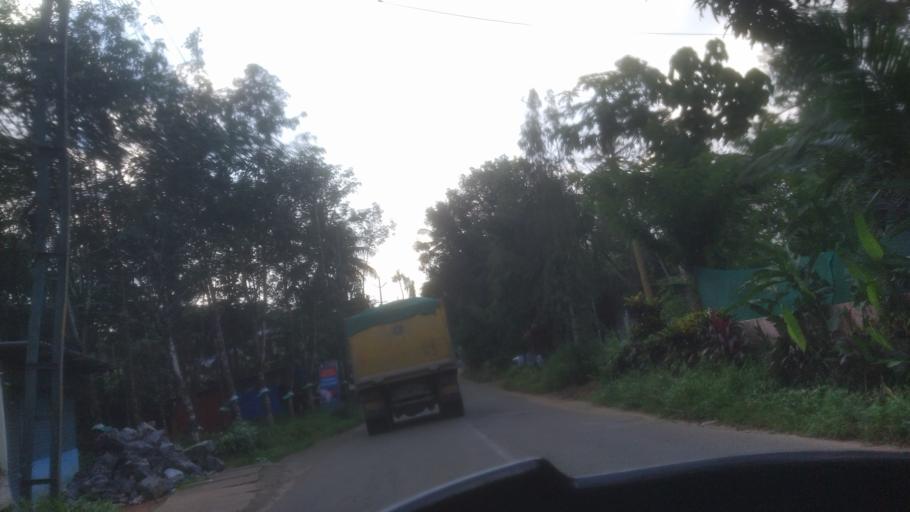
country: IN
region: Kerala
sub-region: Ernakulam
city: Kotamangalam
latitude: 10.0046
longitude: 76.6851
